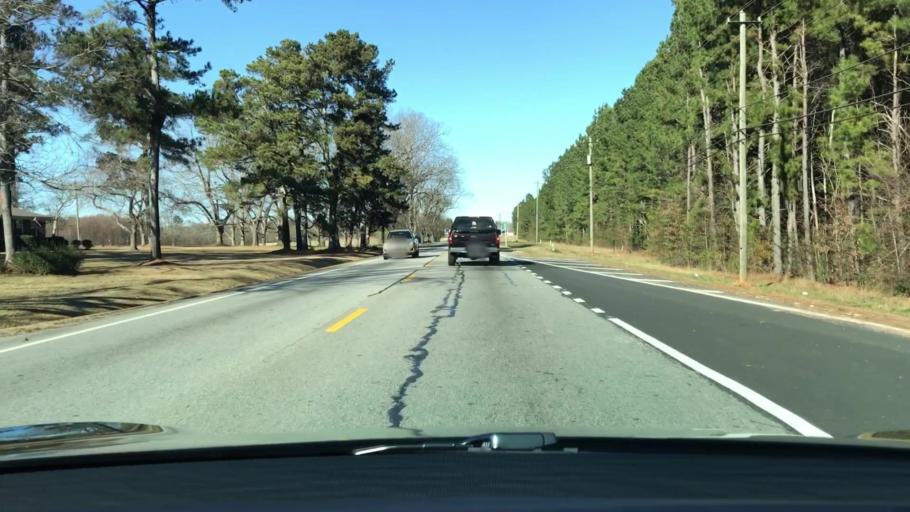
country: US
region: Georgia
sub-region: Walton County
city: Monroe
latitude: 33.8268
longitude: -83.7323
